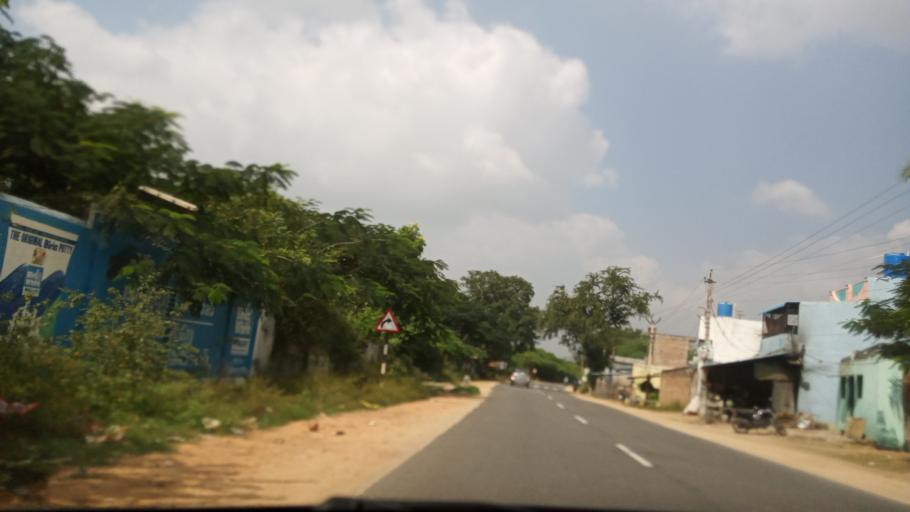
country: IN
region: Andhra Pradesh
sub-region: Chittoor
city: Madanapalle
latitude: 13.6353
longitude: 78.5546
